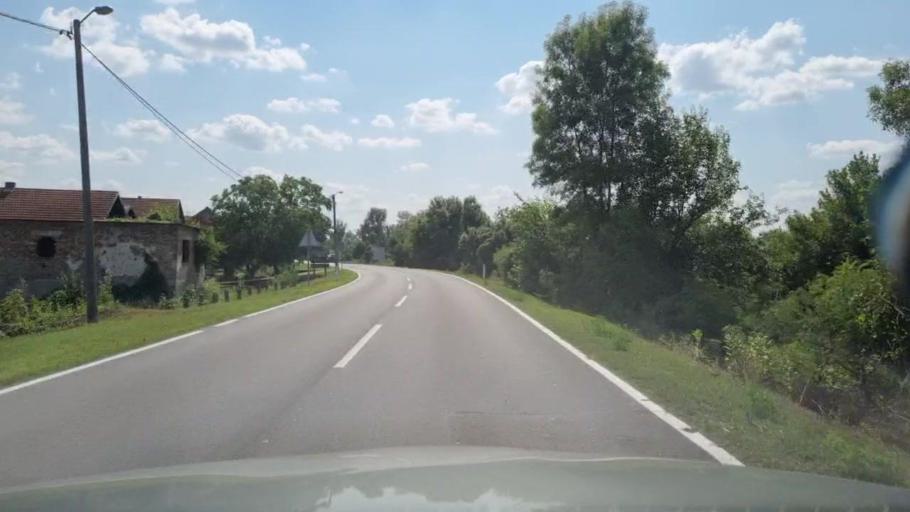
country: HR
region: Brodsko-Posavska
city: Krusevica
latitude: 45.0394
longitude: 18.5276
